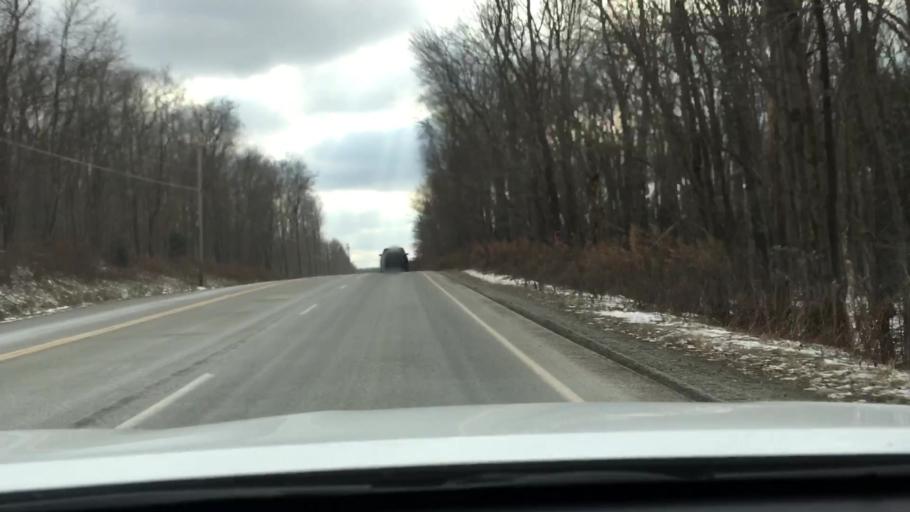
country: US
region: Pennsylvania
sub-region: Lackawanna County
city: Moscow
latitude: 41.2428
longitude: -75.5015
